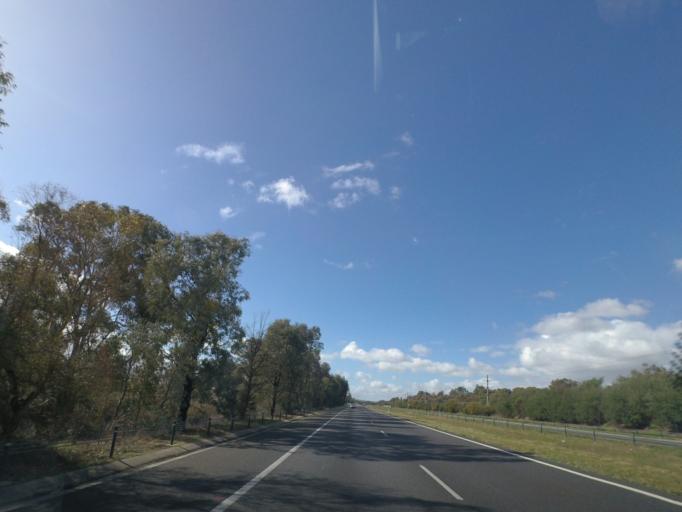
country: AU
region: New South Wales
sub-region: Albury Municipality
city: Lavington
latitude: -36.0576
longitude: 146.9507
